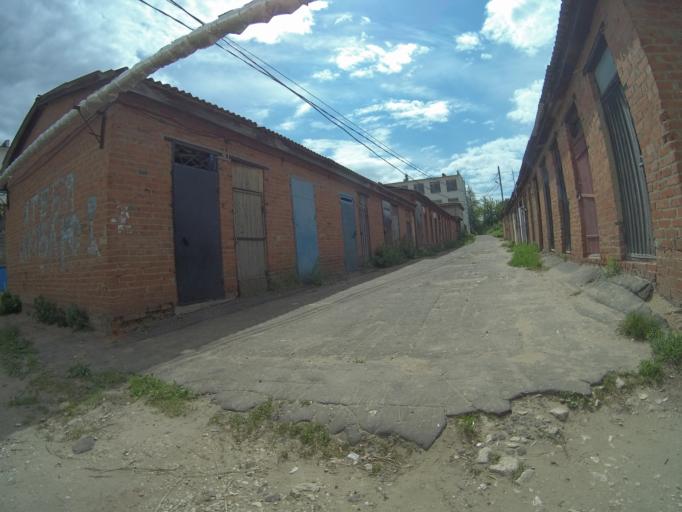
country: RU
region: Vladimir
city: Bogolyubovo
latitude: 56.2118
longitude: 40.5227
